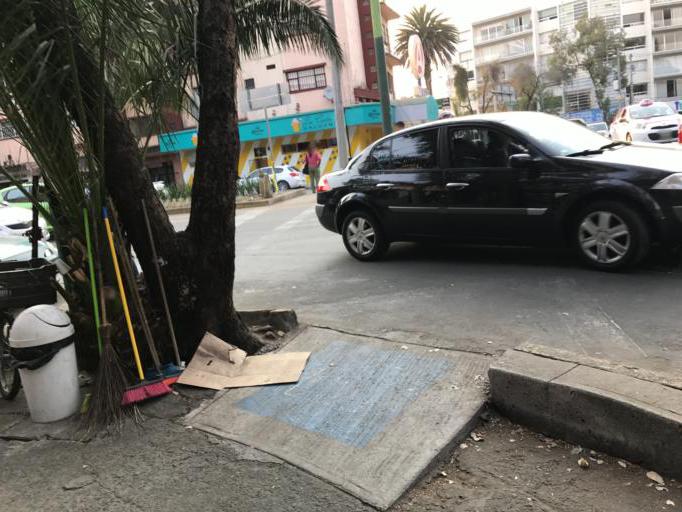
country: MX
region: Mexico City
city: Benito Juarez
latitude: 19.3912
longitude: -99.1511
